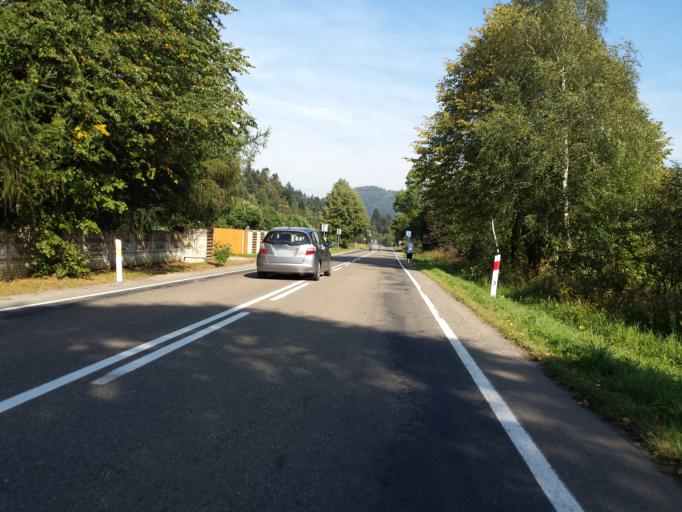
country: PL
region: Subcarpathian Voivodeship
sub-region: Powiat leski
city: Baligrod
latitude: 49.2772
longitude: 22.2832
